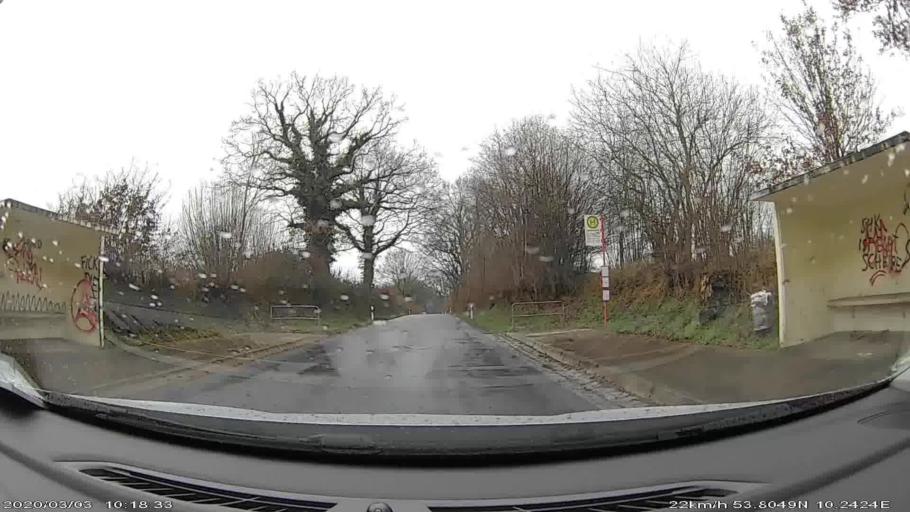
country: DE
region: Schleswig-Holstein
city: Sulfeld
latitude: 53.8027
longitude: 10.2427
